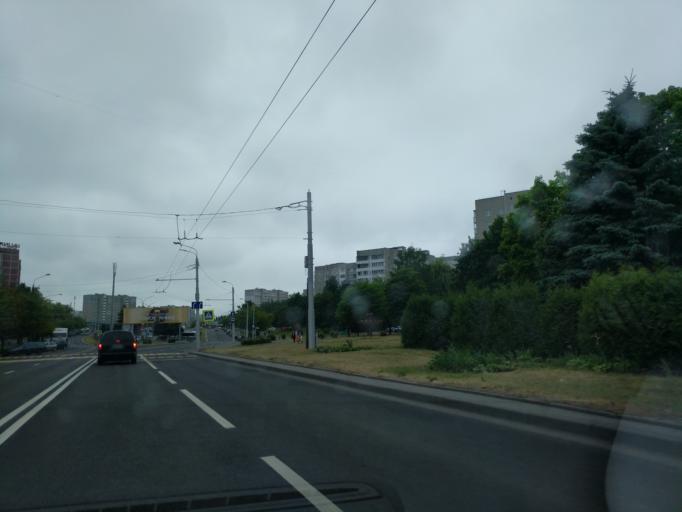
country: BY
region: Minsk
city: Novoye Medvezhino
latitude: 53.8632
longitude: 27.4668
